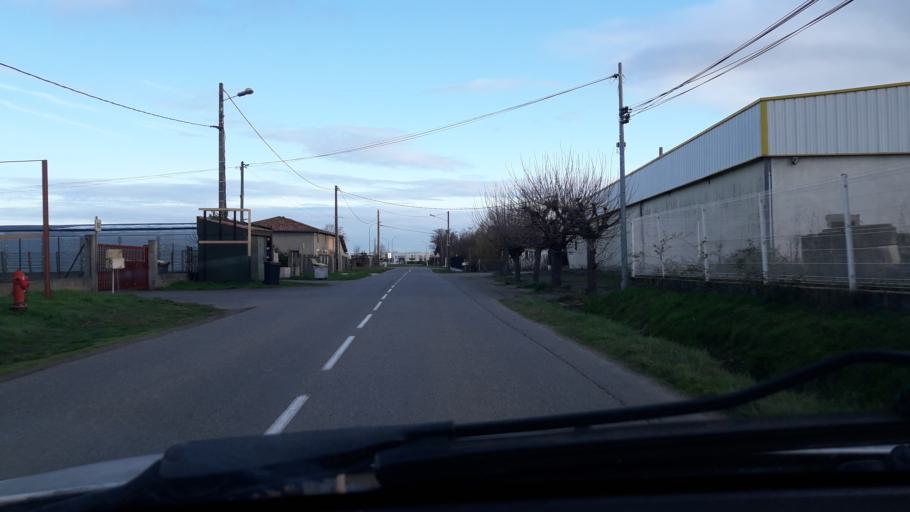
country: FR
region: Midi-Pyrenees
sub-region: Departement de la Haute-Garonne
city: Carbonne
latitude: 43.3074
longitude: 1.2224
